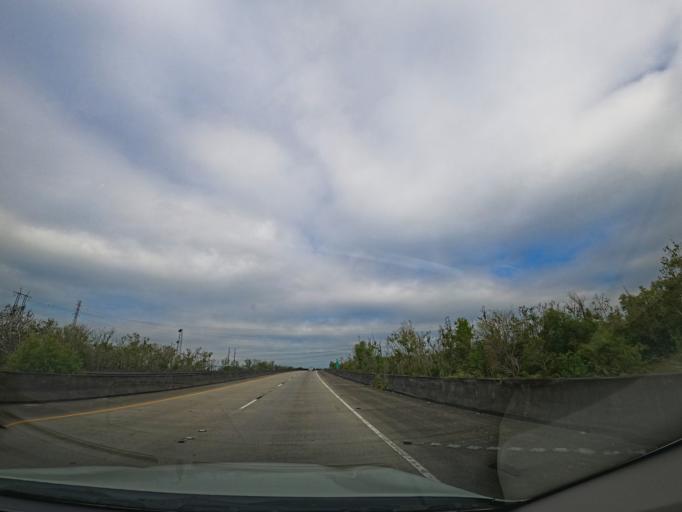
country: US
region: Louisiana
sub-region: Saint Mary Parish
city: Amelia
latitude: 29.6762
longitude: -91.1336
